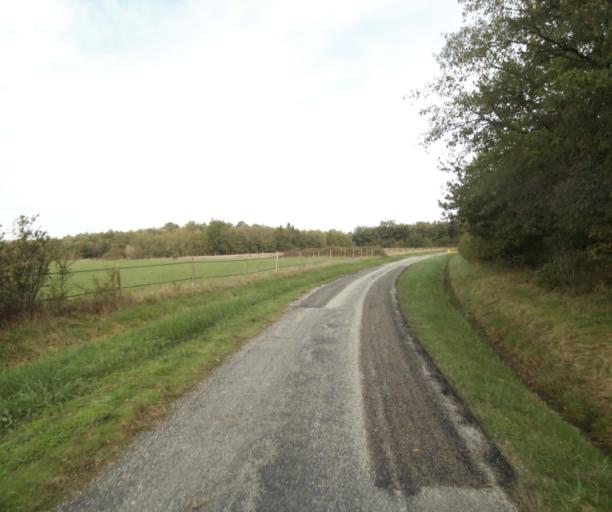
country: FR
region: Midi-Pyrenees
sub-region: Departement du Tarn-et-Garonne
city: Orgueil
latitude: 43.8794
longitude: 1.3877
